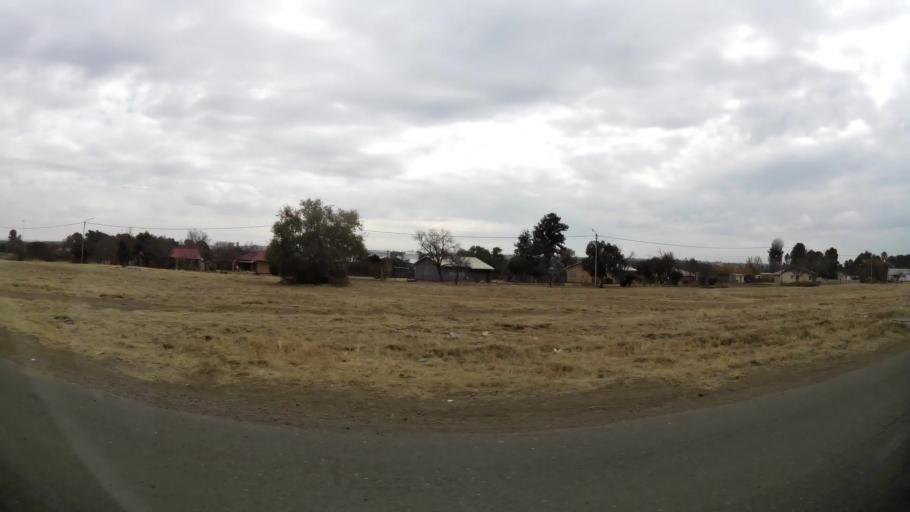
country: ZA
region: Orange Free State
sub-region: Fezile Dabi District Municipality
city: Kroonstad
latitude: -27.6811
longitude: 27.2305
